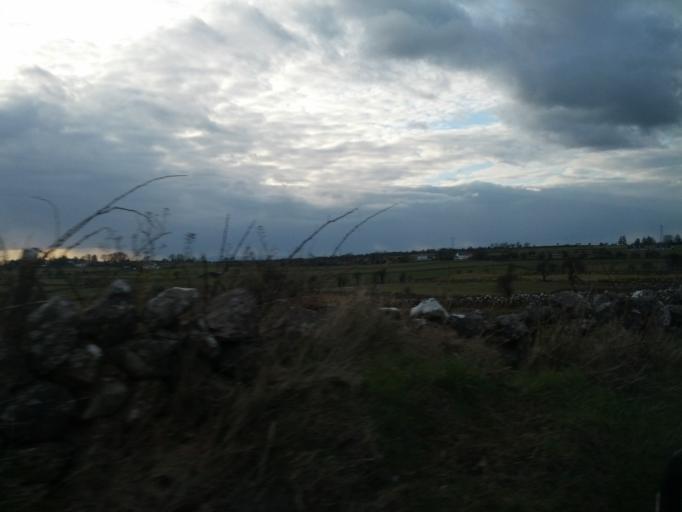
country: IE
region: Connaught
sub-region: County Galway
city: Athenry
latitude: 53.3954
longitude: -8.7469
